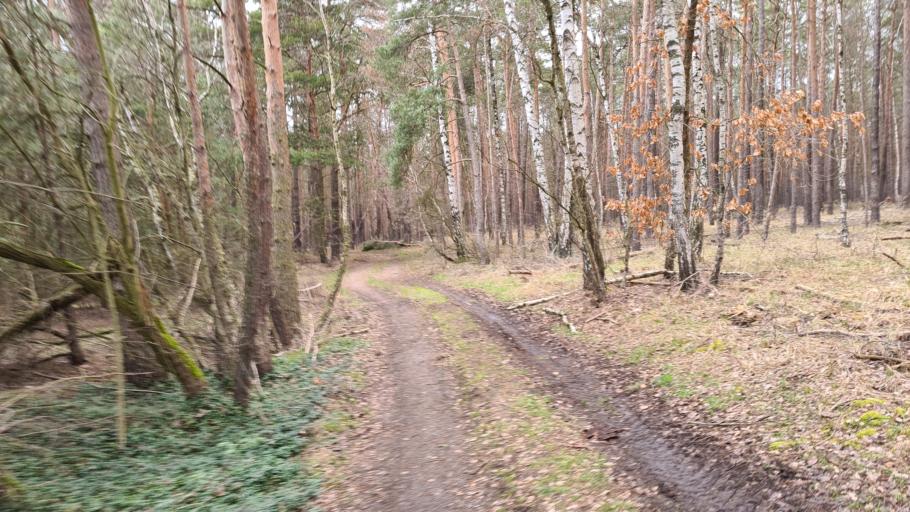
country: DE
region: Brandenburg
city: Schilda
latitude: 51.6100
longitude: 13.4034
